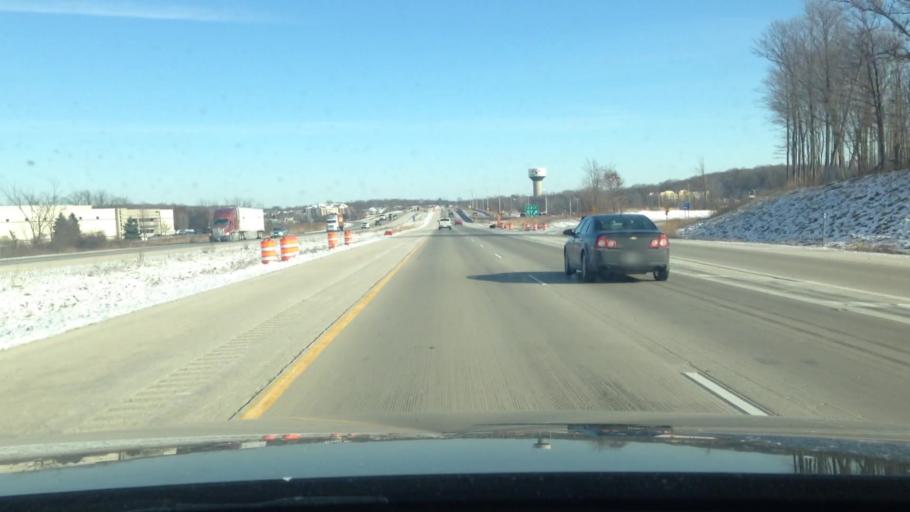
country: US
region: Wisconsin
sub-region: Waukesha County
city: New Berlin
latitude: 42.9489
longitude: -88.1160
